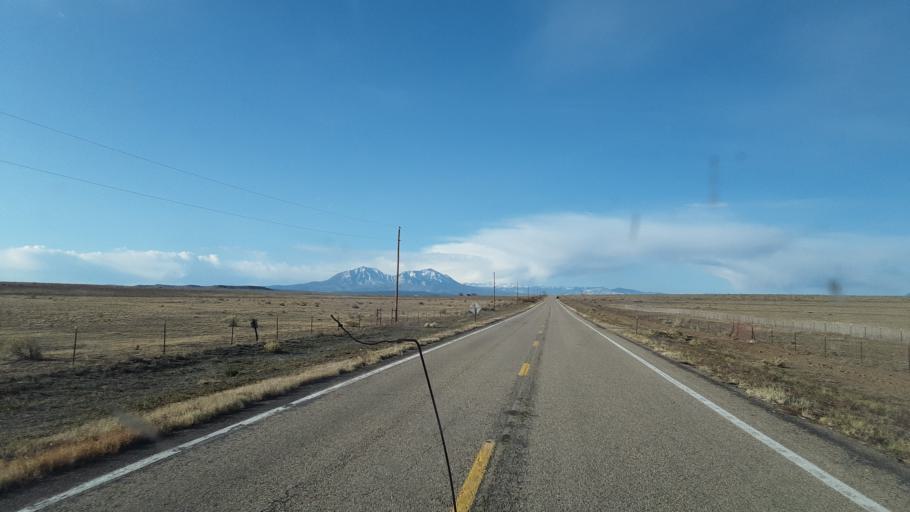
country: US
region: Colorado
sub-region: Huerfano County
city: Walsenburg
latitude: 37.6770
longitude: -104.6587
